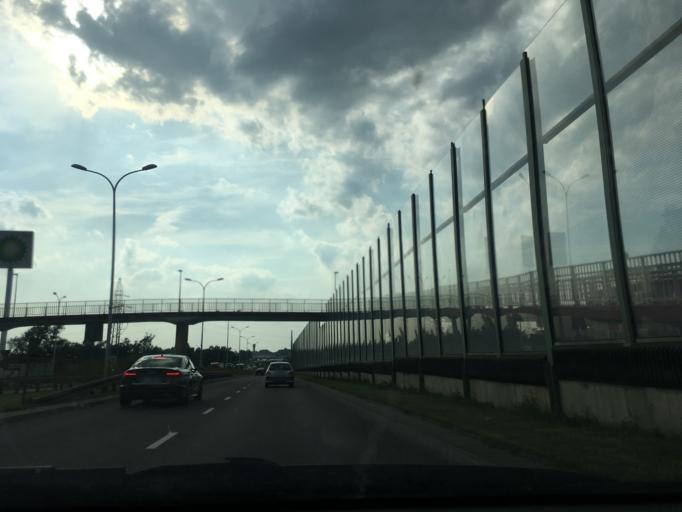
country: PL
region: Podlasie
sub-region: Bialystok
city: Bialystok
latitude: 53.1599
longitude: 23.1154
